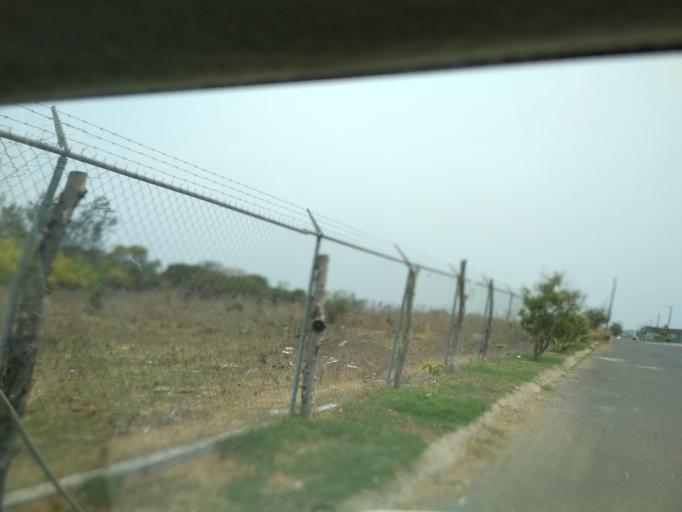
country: MX
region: Veracruz
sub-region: Veracruz
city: Las Amapolas
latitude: 19.1537
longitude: -96.2139
